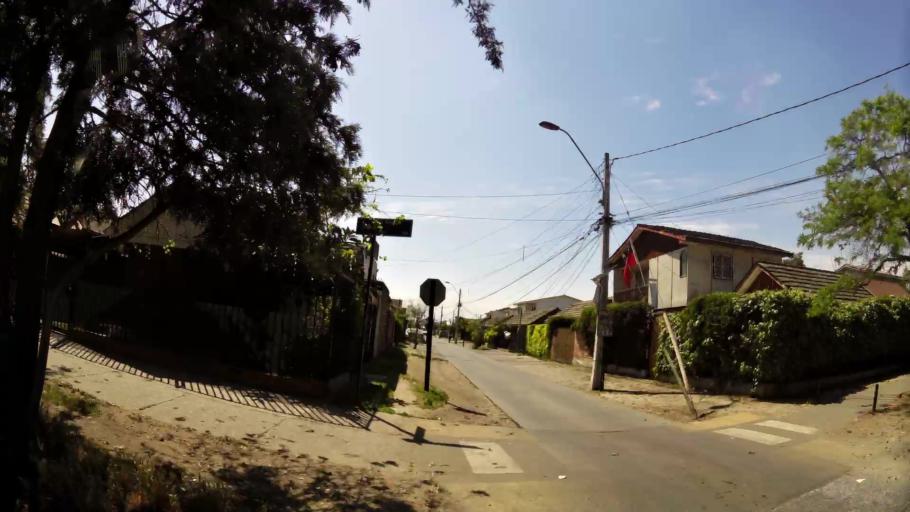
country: CL
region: Santiago Metropolitan
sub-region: Provincia de Santiago
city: La Pintana
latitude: -33.5291
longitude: -70.6447
